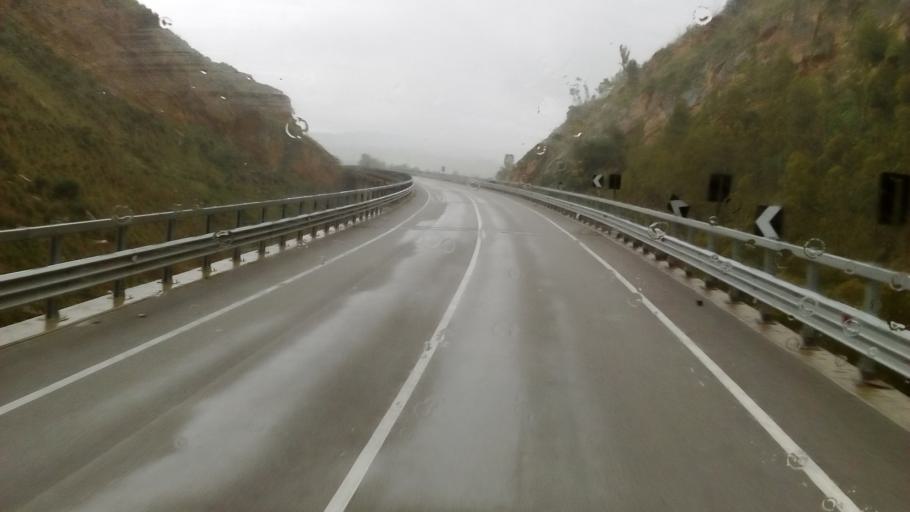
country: IT
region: Sicily
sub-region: Enna
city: Pietraperzia
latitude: 37.4990
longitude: 14.1418
